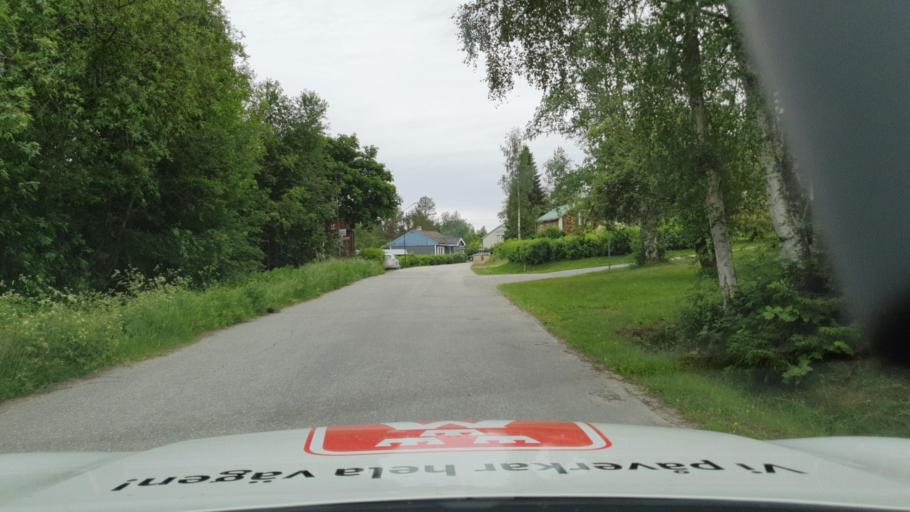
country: SE
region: Vaesterbotten
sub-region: Nordmalings Kommun
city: Nordmaling
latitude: 63.5343
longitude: 19.4428
